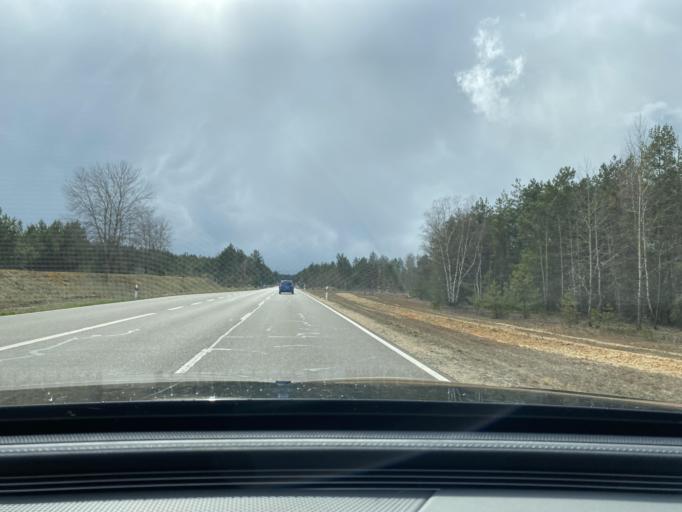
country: DE
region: Saxony
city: Boxberg
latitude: 51.4189
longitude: 14.5974
